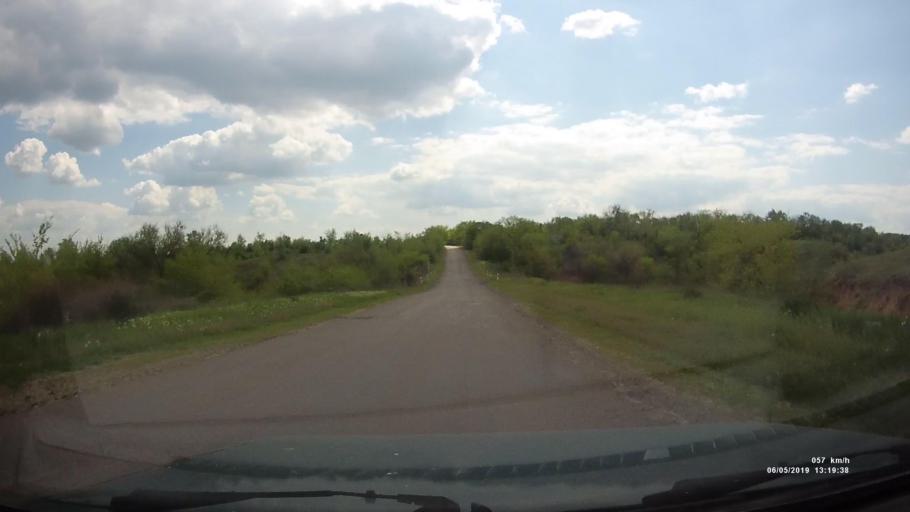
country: RU
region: Rostov
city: Ust'-Donetskiy
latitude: 47.7237
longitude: 40.9133
